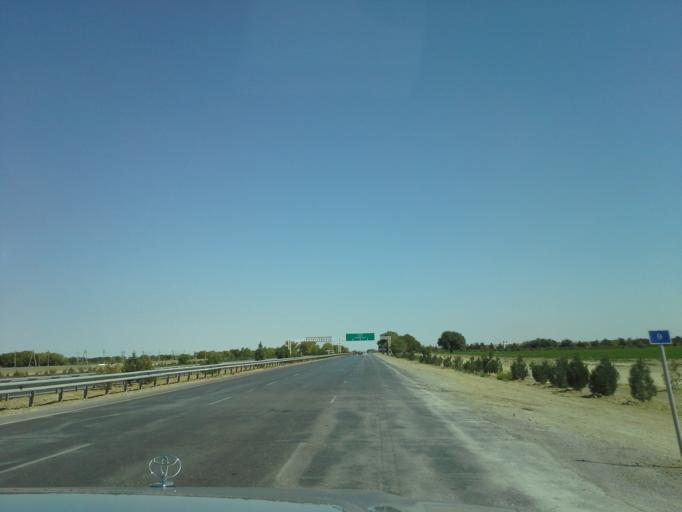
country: TM
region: Ahal
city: Annau
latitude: 37.9040
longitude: 58.5464
